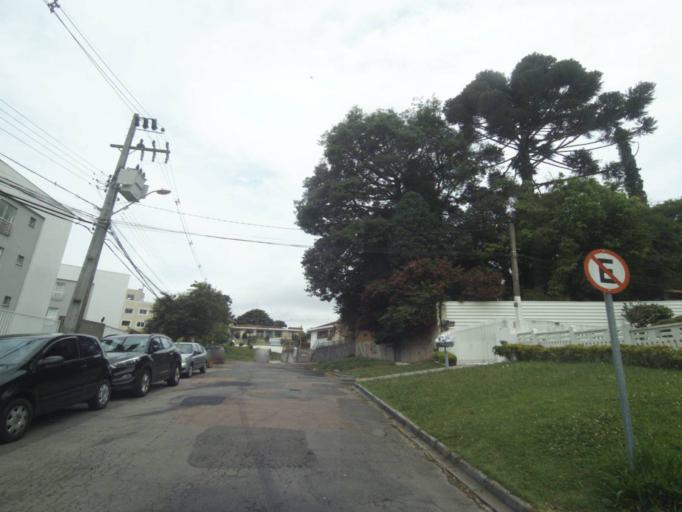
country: BR
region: Parana
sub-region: Curitiba
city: Curitiba
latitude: -25.4151
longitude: -49.2951
